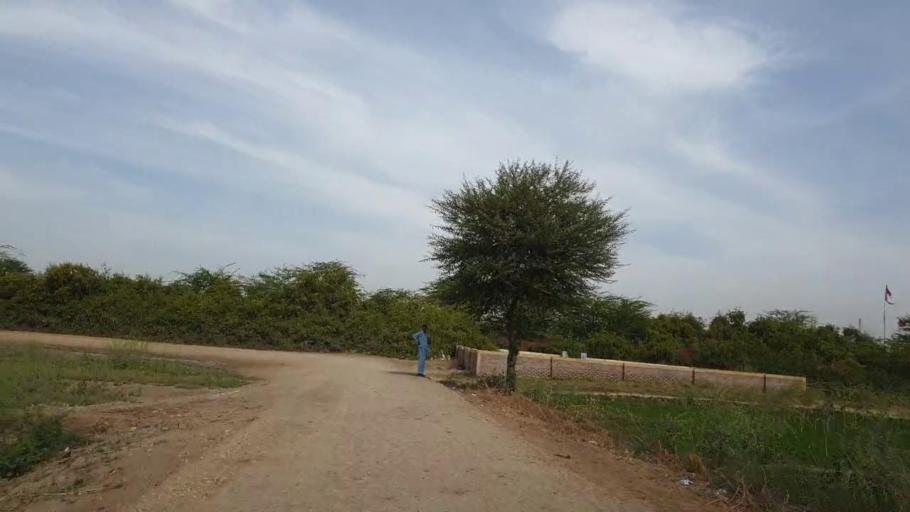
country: PK
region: Sindh
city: Kunri
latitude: 25.1882
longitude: 69.6016
